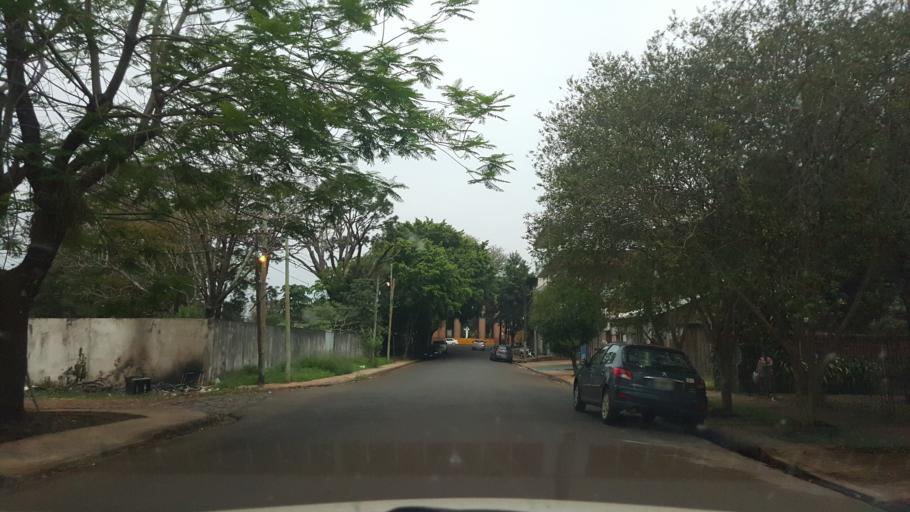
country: AR
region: Misiones
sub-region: Departamento de Capital
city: Posadas
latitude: -27.3784
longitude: -55.9123
